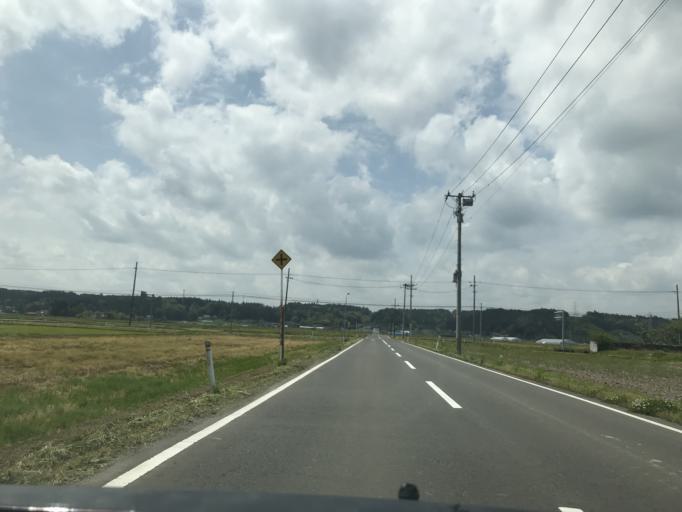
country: JP
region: Miyagi
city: Furukawa
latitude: 38.7487
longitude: 140.9347
